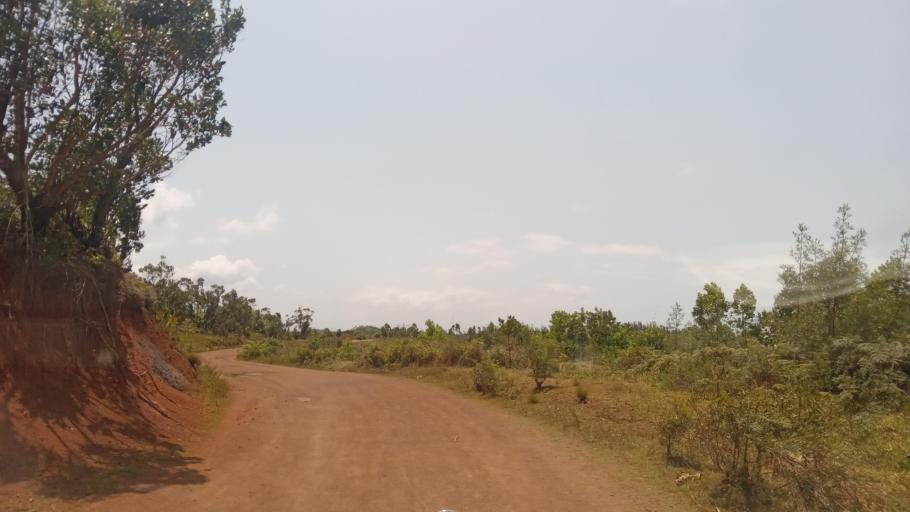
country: MG
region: Atsimo-Atsinanana
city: Vohipaho
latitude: -23.7231
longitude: 47.5656
